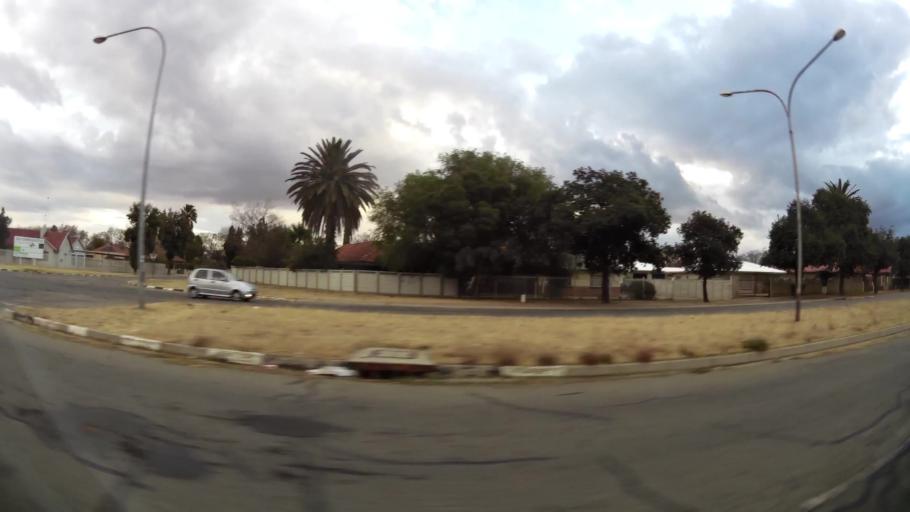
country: ZA
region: Orange Free State
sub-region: Lejweleputswa District Municipality
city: Welkom
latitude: -27.9670
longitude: 26.7421
